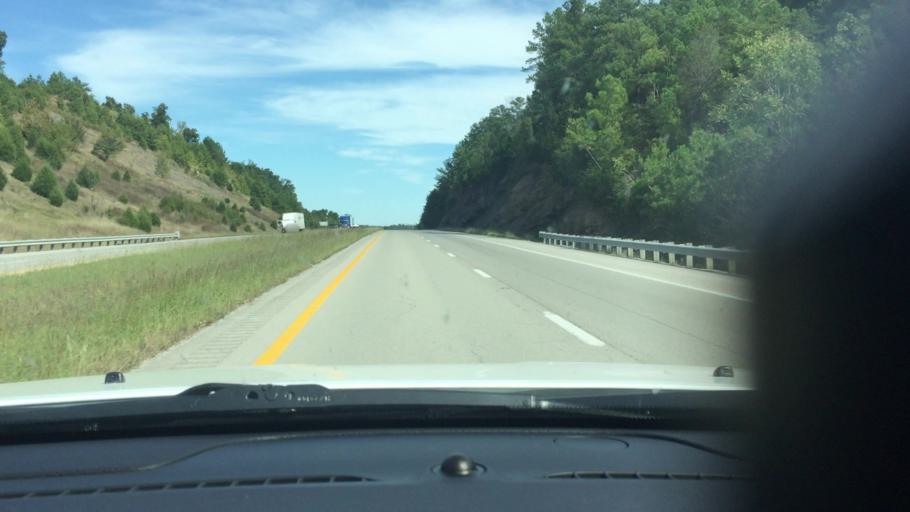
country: US
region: Kentucky
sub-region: Caldwell County
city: Princeton
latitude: 37.1401
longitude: -87.8353
